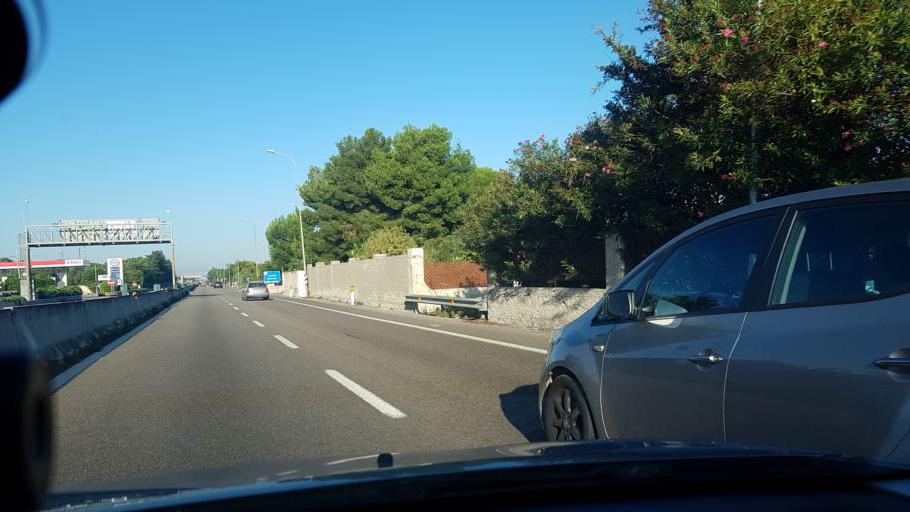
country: IT
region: Apulia
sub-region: Provincia di Bari
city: Parco Scizzo-Parchitello
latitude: 41.0881
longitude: 16.9834
